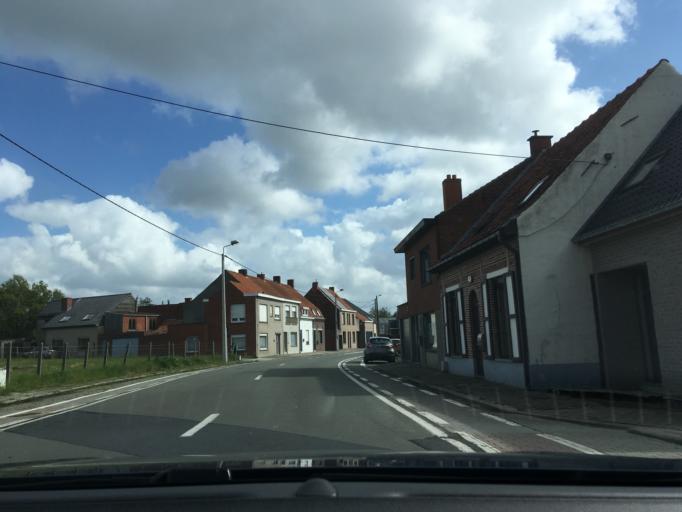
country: BE
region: Flanders
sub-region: Provincie West-Vlaanderen
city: Tielt
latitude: 51.0048
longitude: 3.3251
